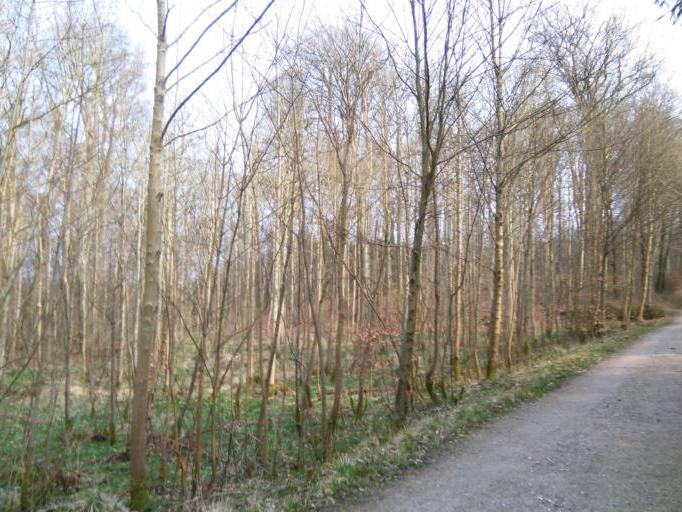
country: DK
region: Central Jutland
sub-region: Arhus Kommune
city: Beder
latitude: 56.0690
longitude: 10.2466
